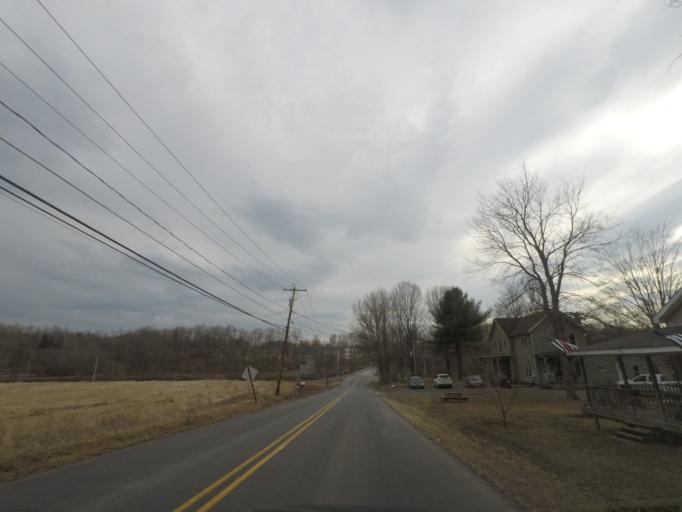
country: US
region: New York
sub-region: Saratoga County
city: Stillwater
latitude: 42.9198
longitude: -73.5135
